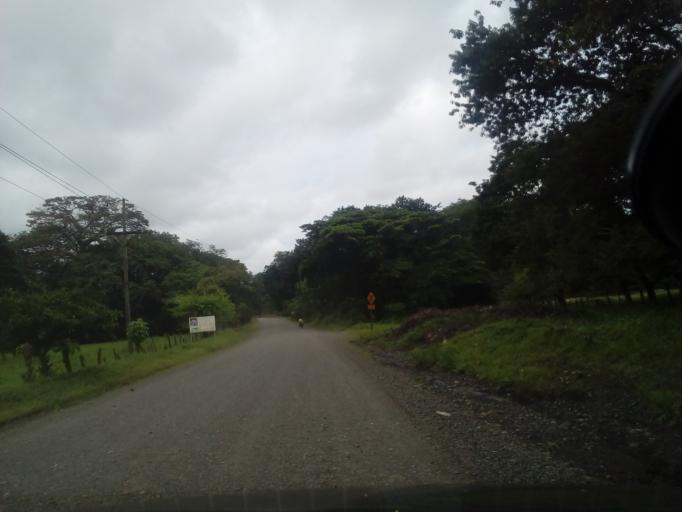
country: CR
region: Guanacaste
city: Samara
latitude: 9.9151
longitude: -85.6281
